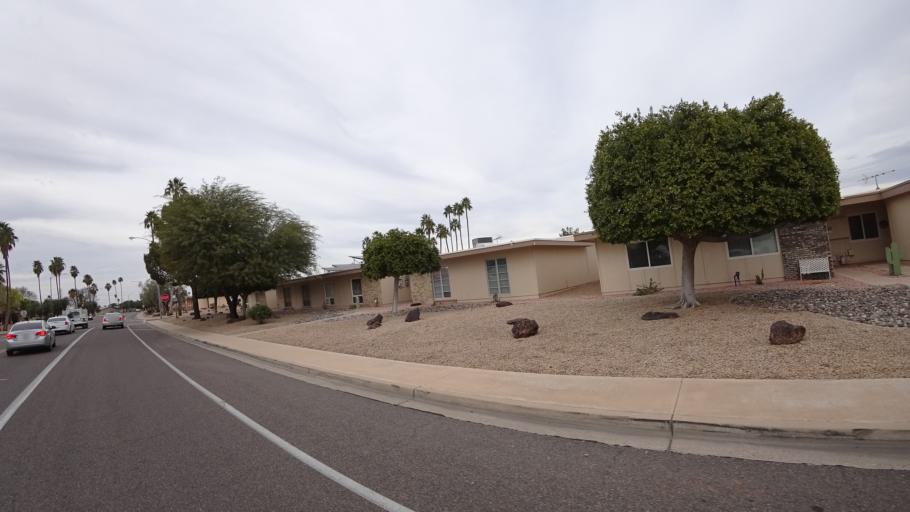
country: US
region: Arizona
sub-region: Maricopa County
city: Youngtown
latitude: 33.6086
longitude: -112.2969
